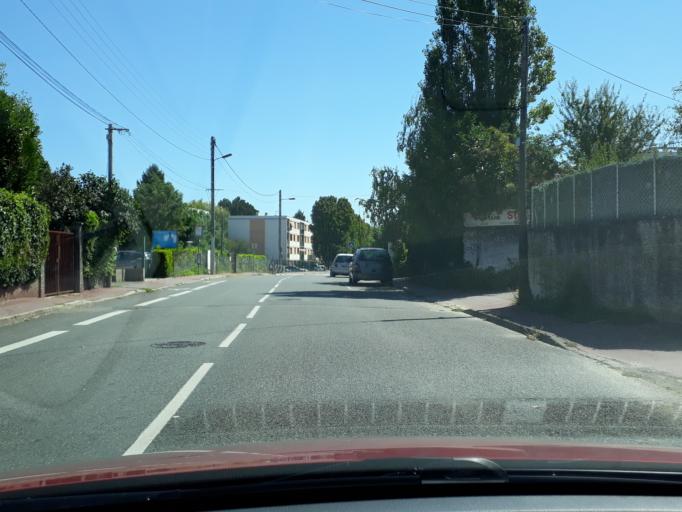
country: FR
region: Rhone-Alpes
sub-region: Departement du Rhone
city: Saint-Priest
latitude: 45.6977
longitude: 4.9522
